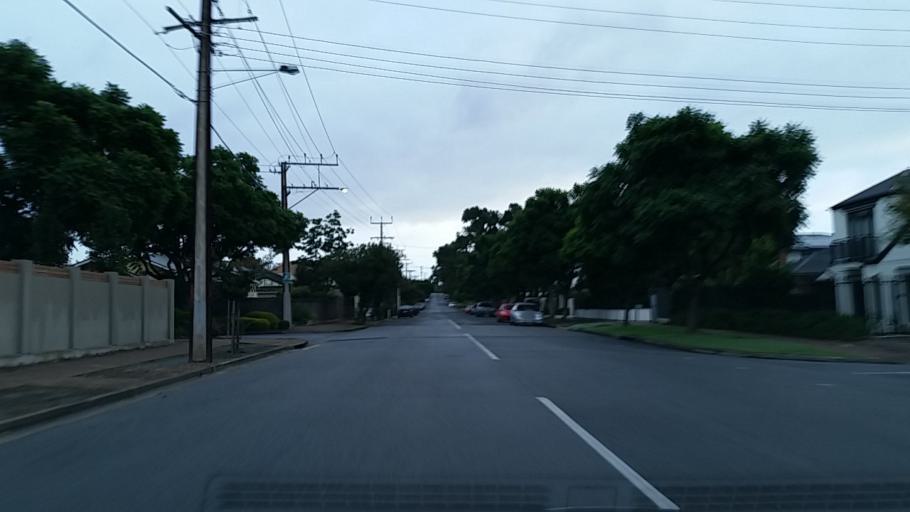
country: AU
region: South Australia
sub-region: Port Adelaide Enfield
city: Klemzig
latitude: -34.8875
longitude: 138.6226
